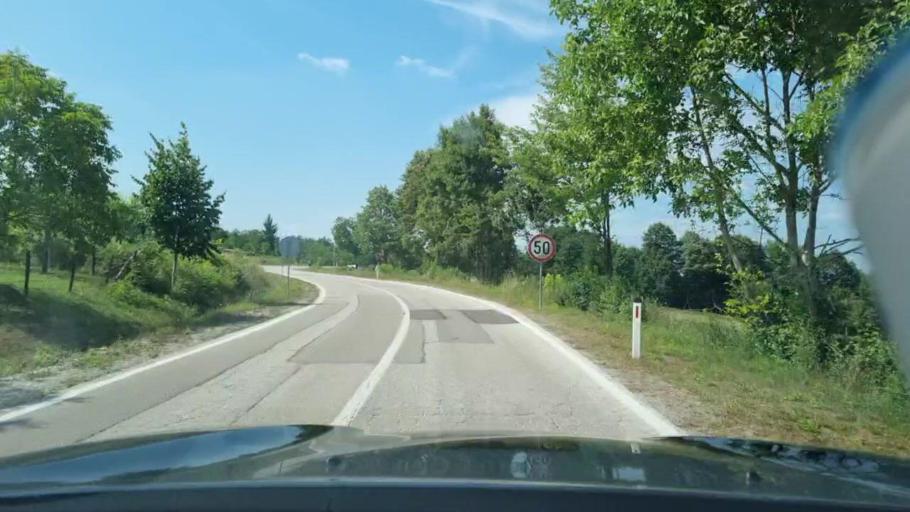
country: BA
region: Federation of Bosnia and Herzegovina
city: Bosanska Krupa
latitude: 44.8358
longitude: 16.1653
